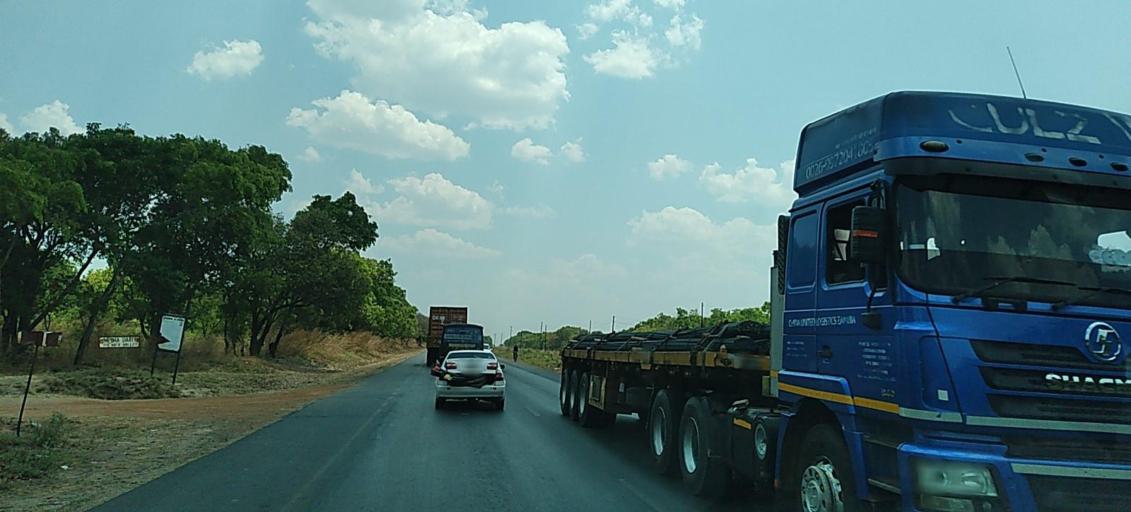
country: ZM
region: Central
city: Kabwe
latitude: -14.3318
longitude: 28.5360
